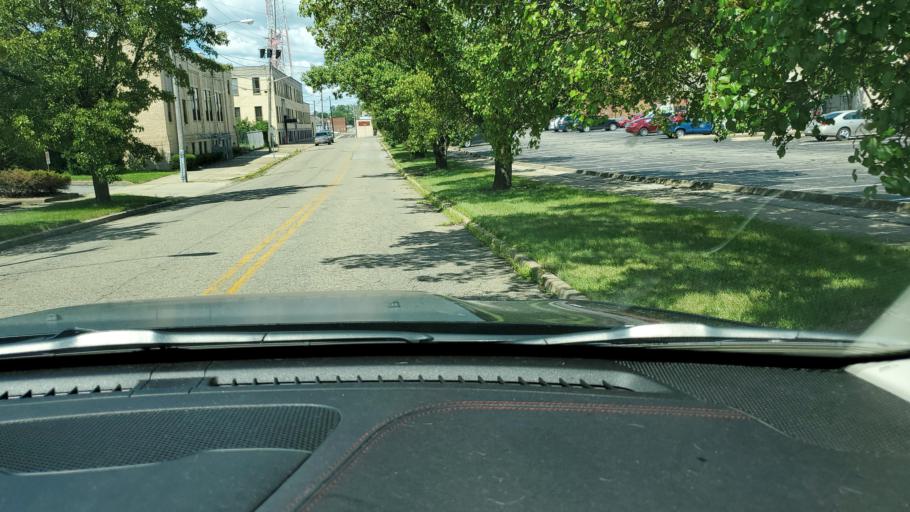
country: US
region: Ohio
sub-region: Trumbull County
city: Warren
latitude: 41.2351
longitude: -80.8140
